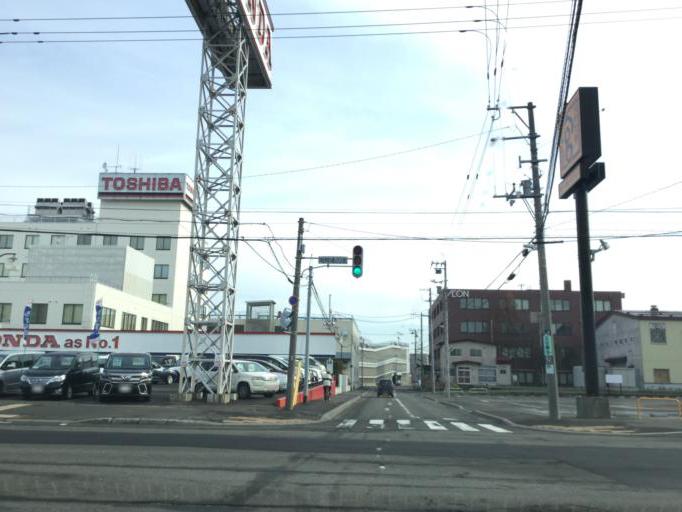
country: JP
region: Hokkaido
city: Sapporo
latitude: 43.0287
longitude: 141.4414
